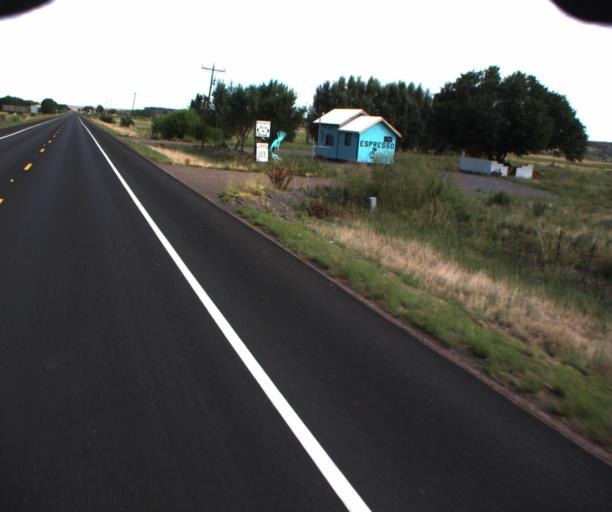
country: US
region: Arizona
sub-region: Apache County
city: Springerville
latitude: 34.1406
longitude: -109.2910
